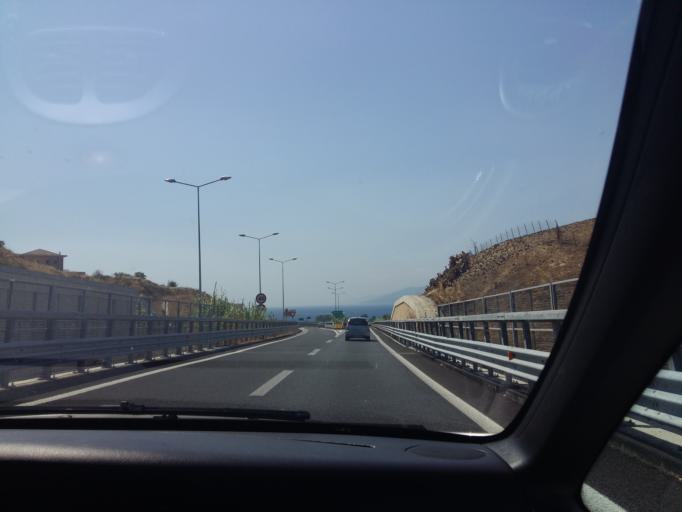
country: IT
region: Calabria
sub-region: Provincia di Reggio Calabria
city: Campo Calabro
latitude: 38.2126
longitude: 15.6458
